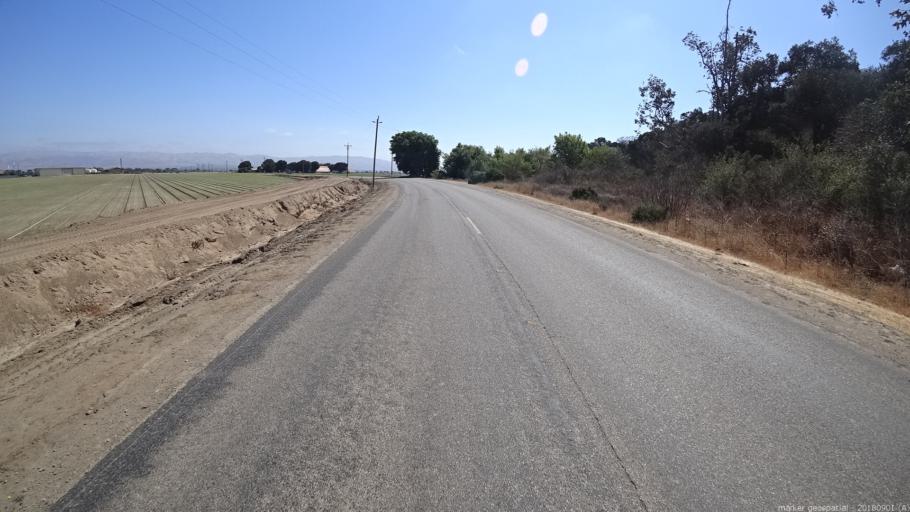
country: US
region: California
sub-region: Monterey County
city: Gonzales
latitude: 36.4778
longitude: -121.4813
